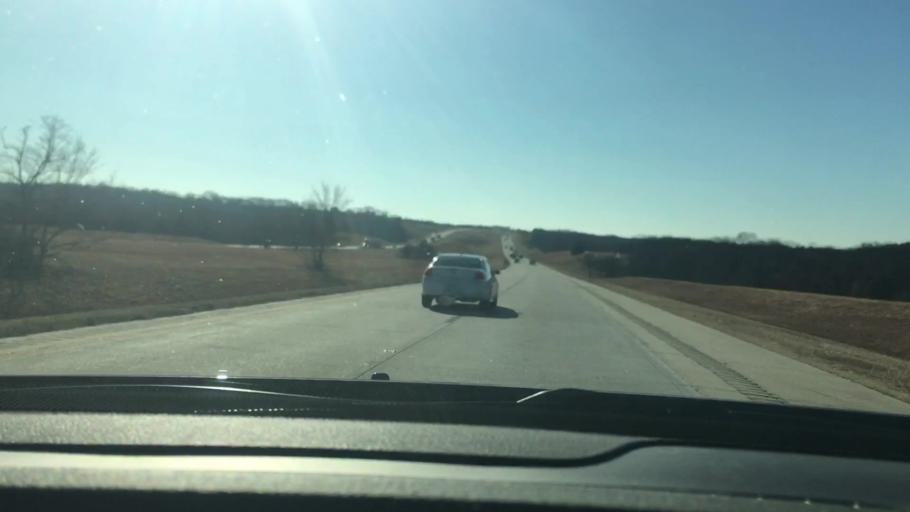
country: US
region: Oklahoma
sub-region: Love County
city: Marietta
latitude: 33.9929
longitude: -97.1403
